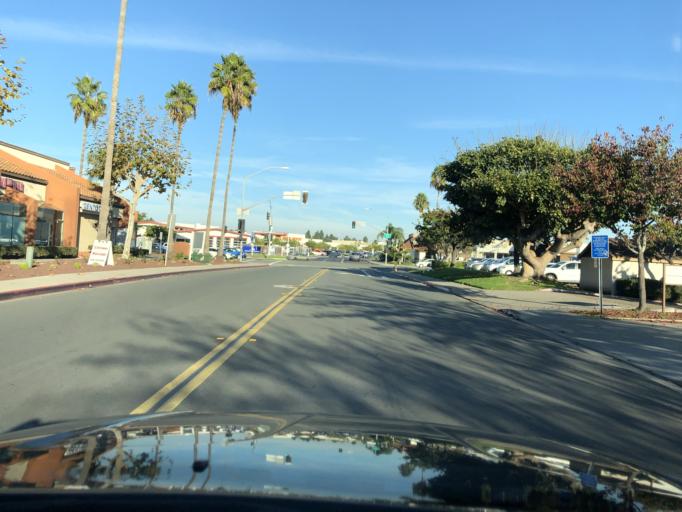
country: US
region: California
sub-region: San Diego County
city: La Jolla
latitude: 32.8211
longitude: -117.1838
